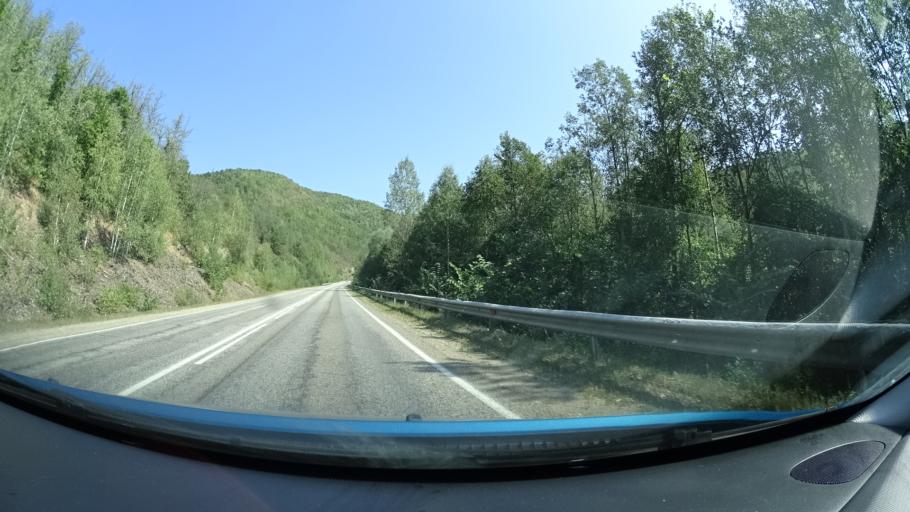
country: RU
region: Bashkortostan
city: Inzer
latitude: 54.3368
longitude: 57.1408
